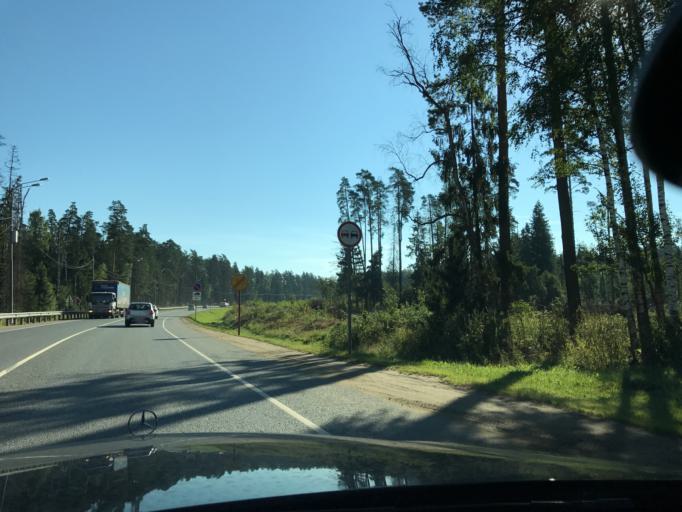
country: RU
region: Moskovskaya
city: Chernogolovka
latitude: 55.9799
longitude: 38.3109
